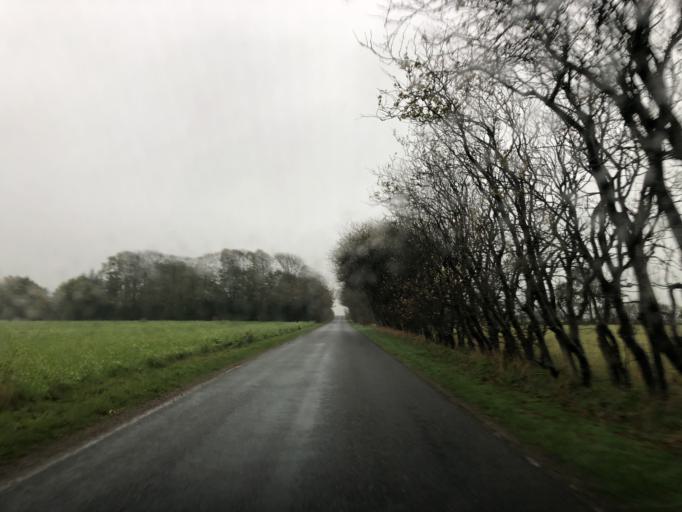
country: DK
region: Central Jutland
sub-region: Herning Kommune
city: Snejbjerg
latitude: 56.0855
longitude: 8.9125
